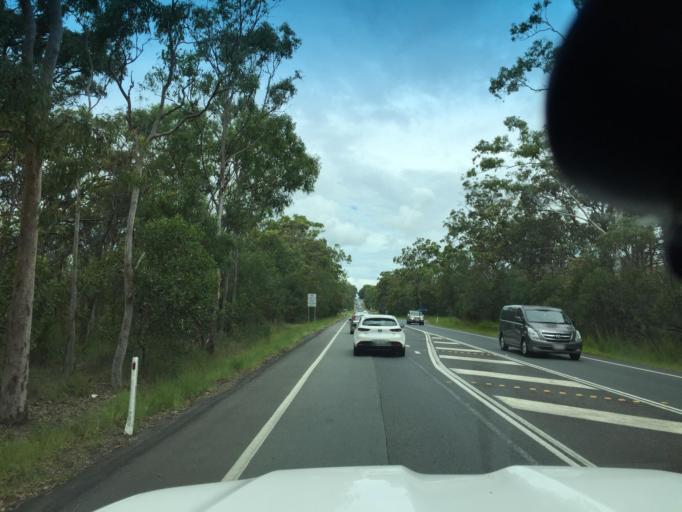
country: AU
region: Queensland
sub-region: Moreton Bay
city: Deception Bay
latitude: -27.1805
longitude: 152.9938
